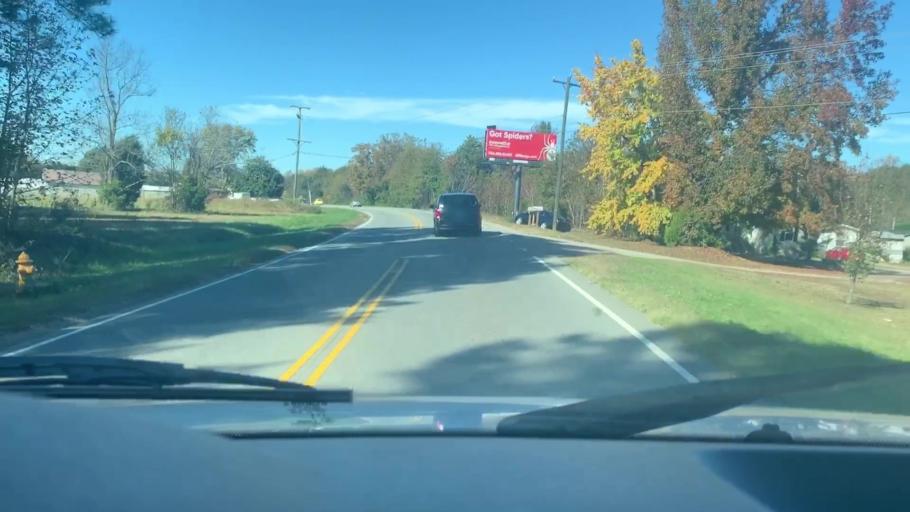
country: US
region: North Carolina
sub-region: Lincoln County
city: Lowesville
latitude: 35.4409
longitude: -80.9812
